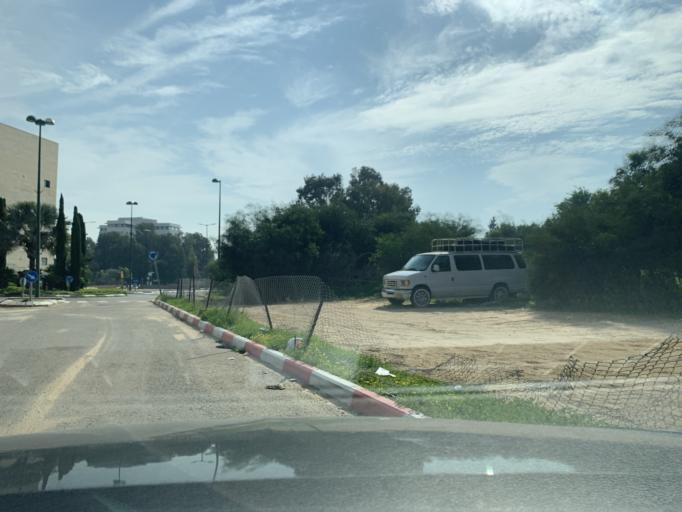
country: IL
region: Central District
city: Ganne Tiqwa
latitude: 32.0510
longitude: 34.8555
